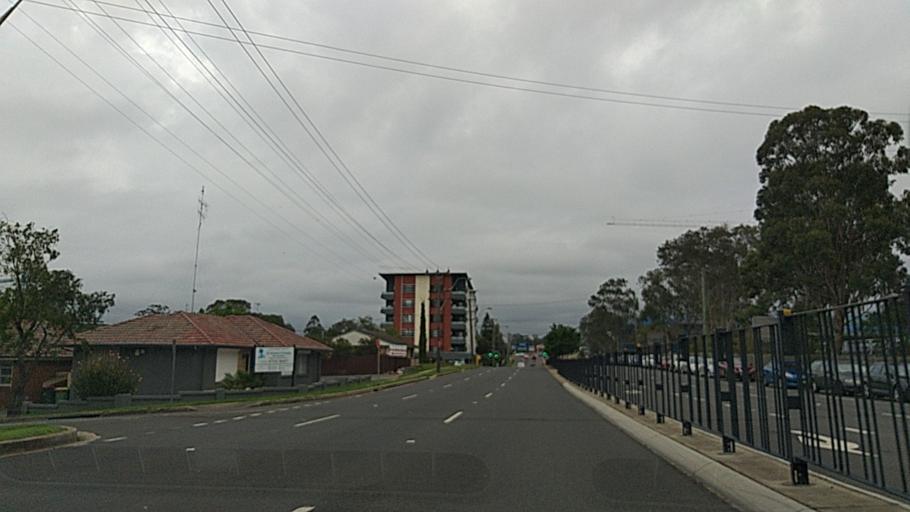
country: AU
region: New South Wales
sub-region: Penrith Municipality
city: Kingswood Park
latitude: -33.7599
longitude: 150.7114
